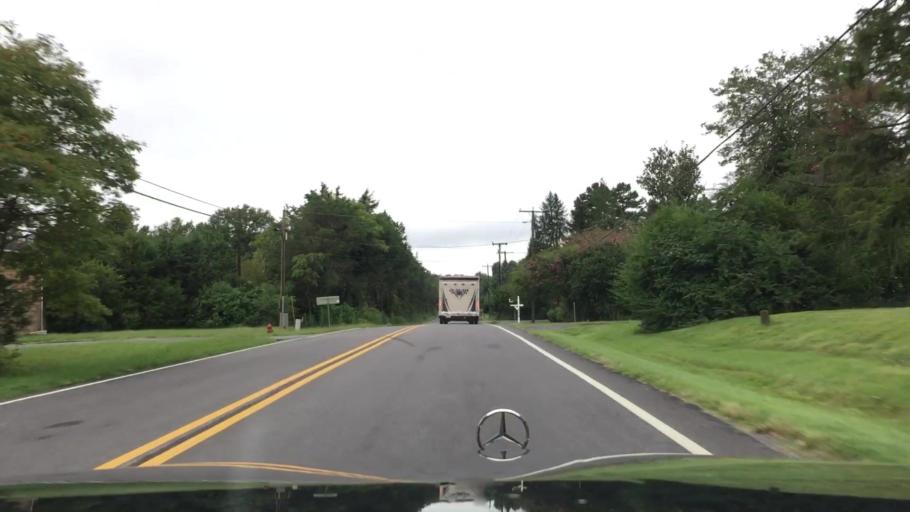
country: US
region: Virginia
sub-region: Orange County
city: Gordonsville
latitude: 38.1376
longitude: -78.1969
